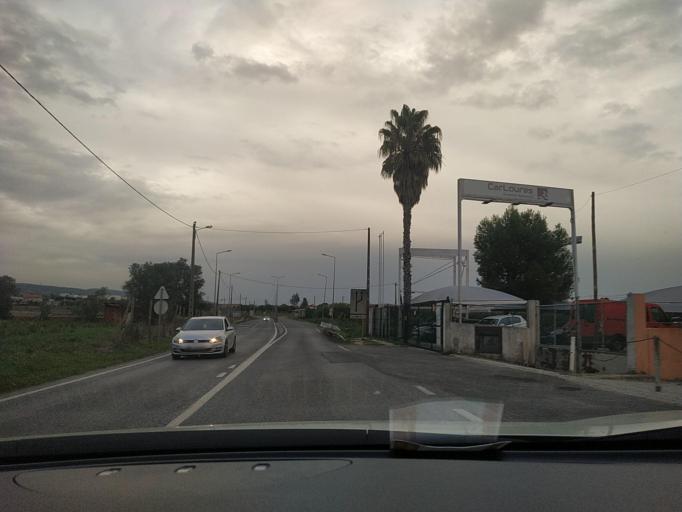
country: PT
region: Lisbon
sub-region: Loures
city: Santo Antao do Tojal
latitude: 38.8524
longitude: -9.1508
